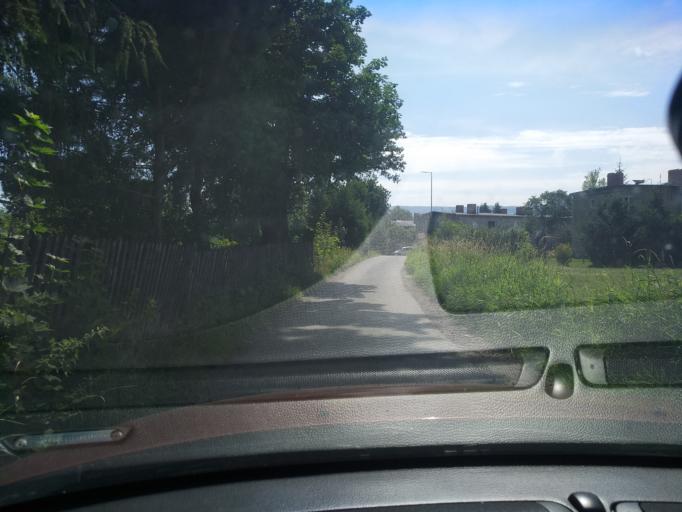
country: PL
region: Lower Silesian Voivodeship
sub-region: Powiat lwowecki
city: Mirsk
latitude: 50.9784
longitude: 15.3447
